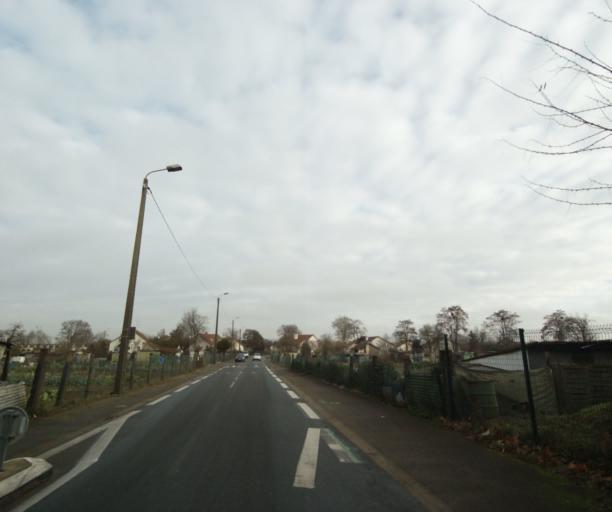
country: FR
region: Pays de la Loire
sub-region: Departement de la Sarthe
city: Allonnes
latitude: 47.9830
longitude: 0.1733
